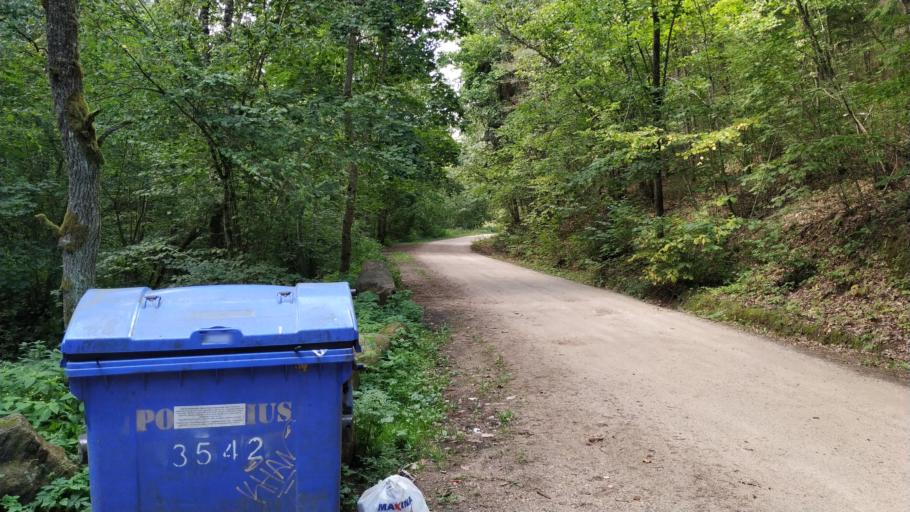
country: LT
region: Vilnius County
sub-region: Vilniaus Rajonas
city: Vievis
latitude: 54.8156
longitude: 24.9643
